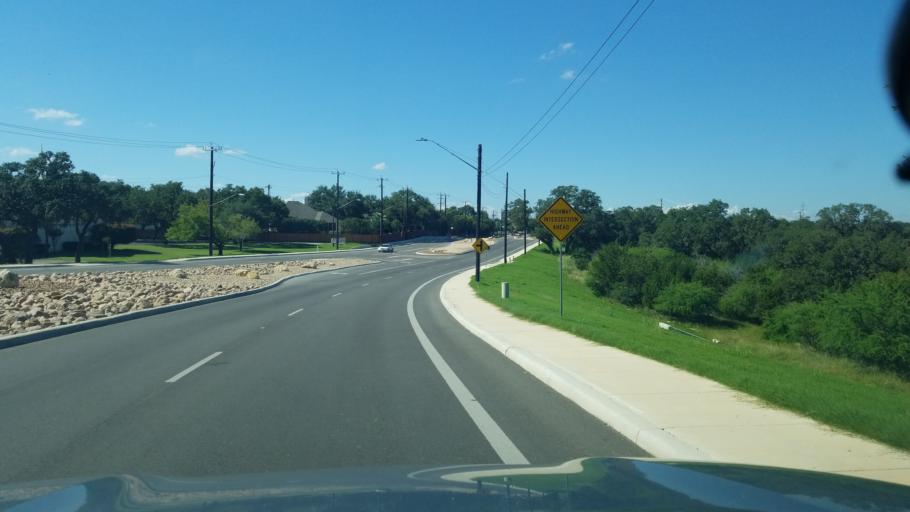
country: US
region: Texas
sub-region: Bexar County
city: Hollywood Park
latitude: 29.5986
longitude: -98.4403
